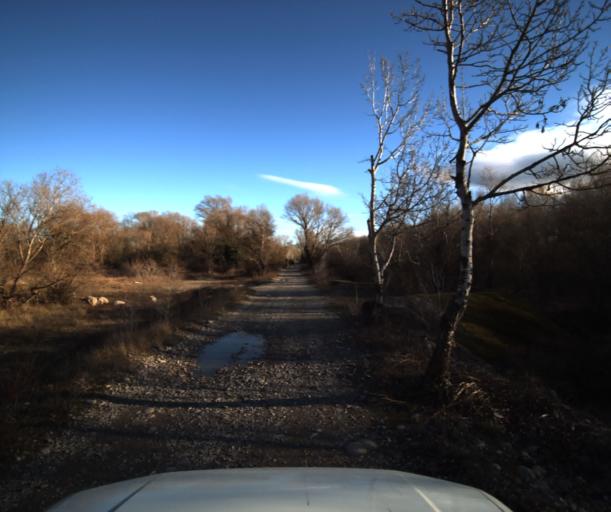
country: FR
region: Provence-Alpes-Cote d'Azur
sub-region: Departement du Vaucluse
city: Pertuis
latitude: 43.6747
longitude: 5.4705
